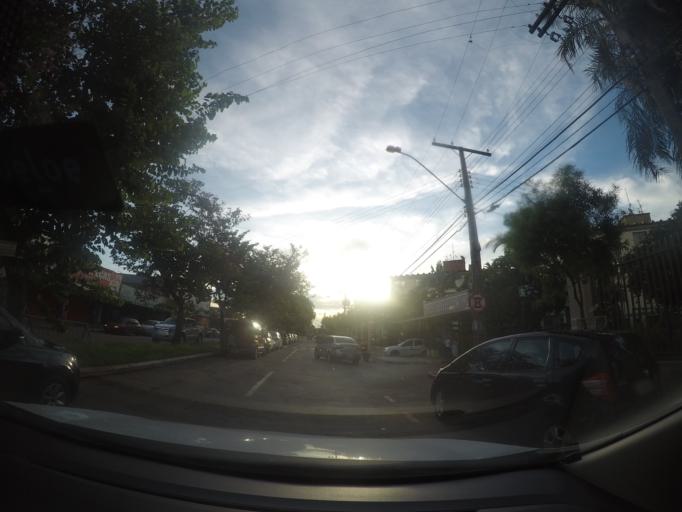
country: BR
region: Goias
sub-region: Goiania
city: Goiania
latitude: -16.6850
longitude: -49.3143
